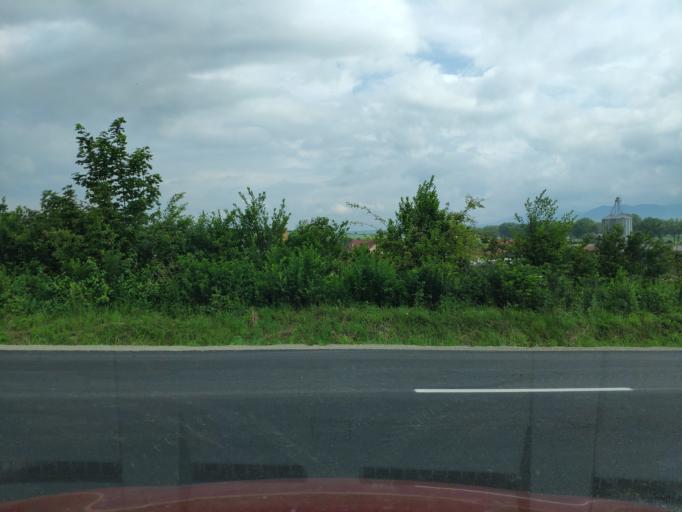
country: SK
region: Kosicky
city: Kosice
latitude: 48.8047
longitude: 21.2975
